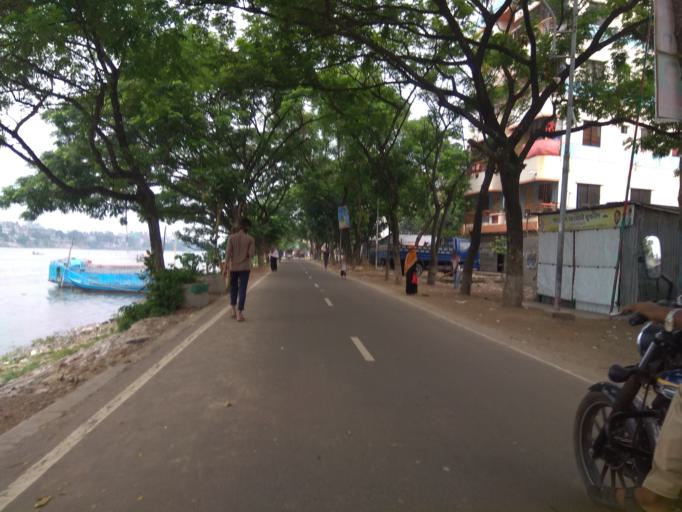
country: BD
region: Dhaka
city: Azimpur
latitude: 23.7087
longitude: 90.3813
